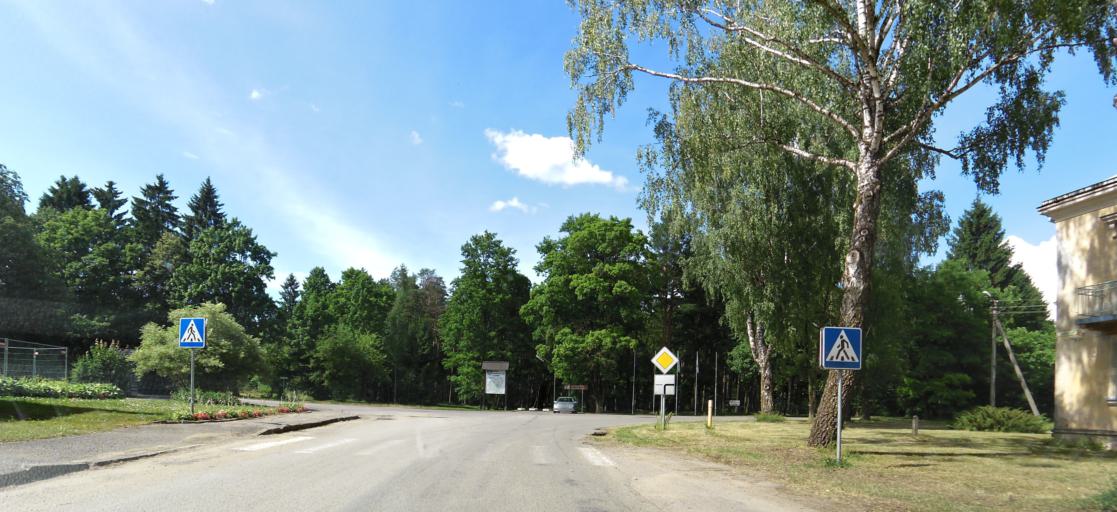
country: LT
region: Panevezys
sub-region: Birzai
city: Birzai
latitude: 56.1972
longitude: 24.6262
